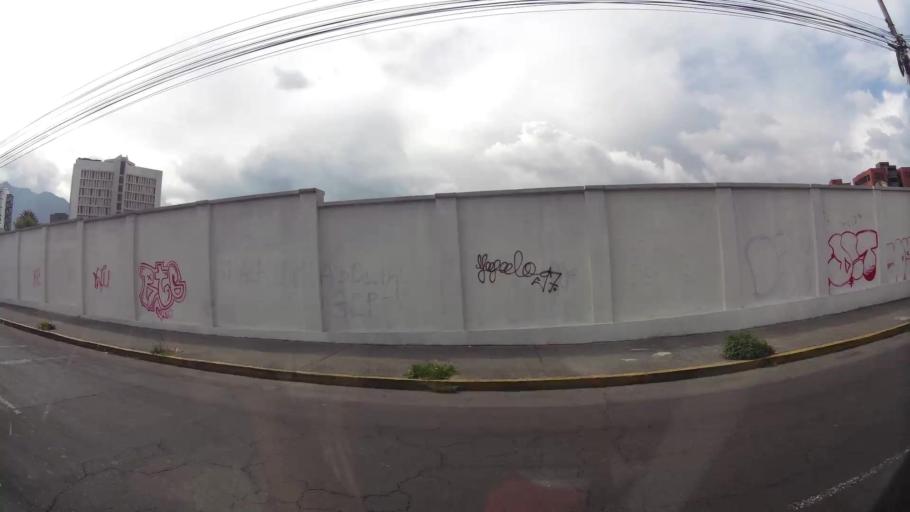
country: EC
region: Pichincha
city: Quito
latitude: -0.2127
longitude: -78.4894
